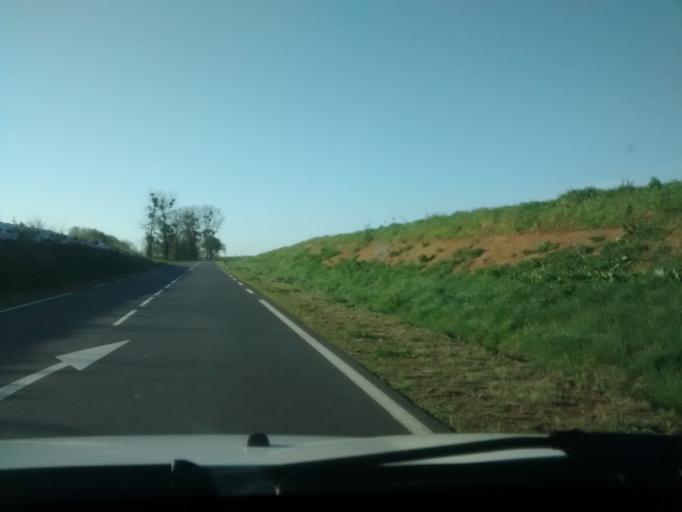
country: FR
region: Brittany
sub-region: Departement d'Ille-et-Vilaine
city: Roz-sur-Couesnon
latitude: 48.5566
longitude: -1.5949
